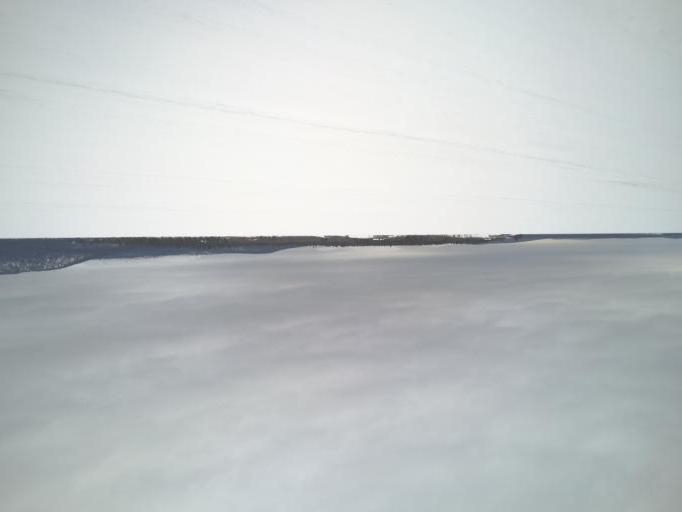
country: FI
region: Lapland
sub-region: Tunturi-Lappi
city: Muonio
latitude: 67.9130
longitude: 24.0532
